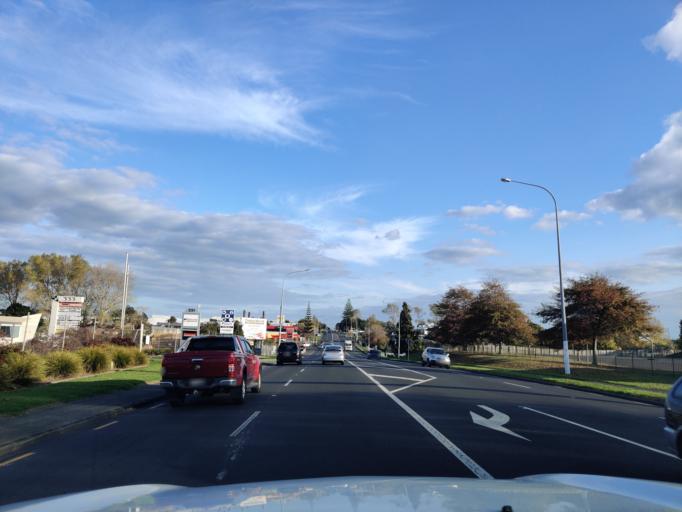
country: NZ
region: Auckland
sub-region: Auckland
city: Manukau City
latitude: -36.9544
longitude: 174.8907
